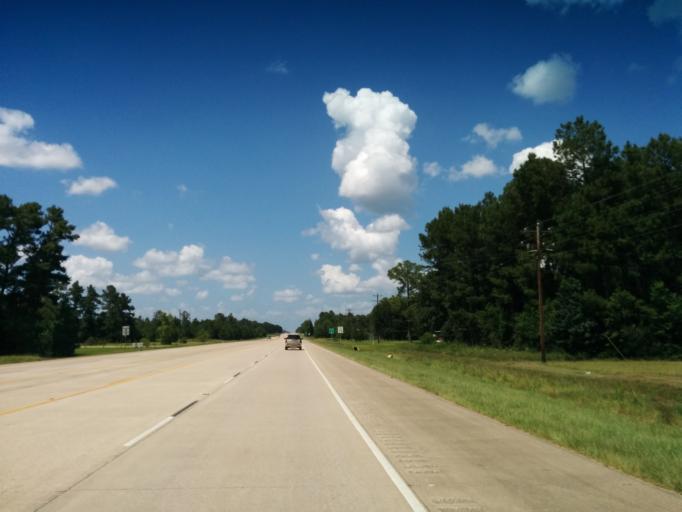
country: US
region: Texas
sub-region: Jasper County
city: Buna
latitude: 30.4692
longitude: -93.9595
